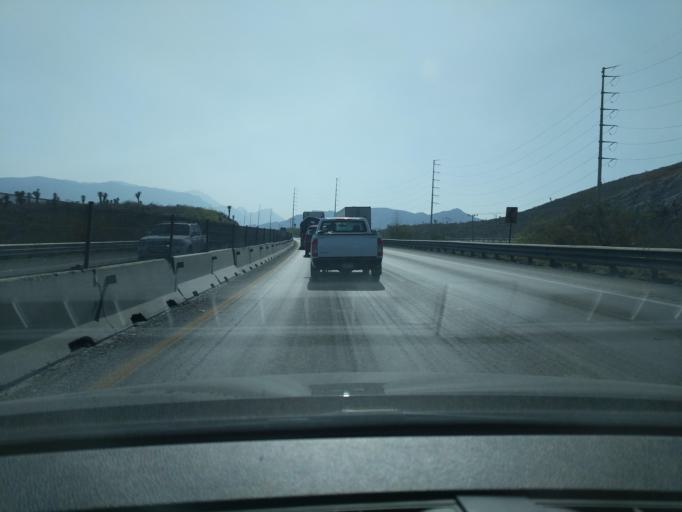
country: MX
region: Nuevo Leon
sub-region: Garcia
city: Los Parques
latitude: 25.7522
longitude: -100.5068
